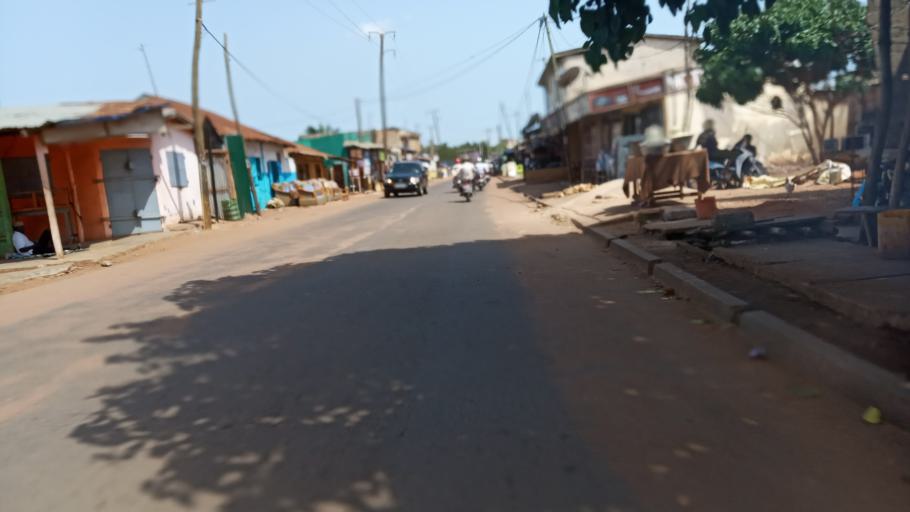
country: TG
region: Maritime
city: Lome
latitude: 6.2232
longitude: 1.2081
